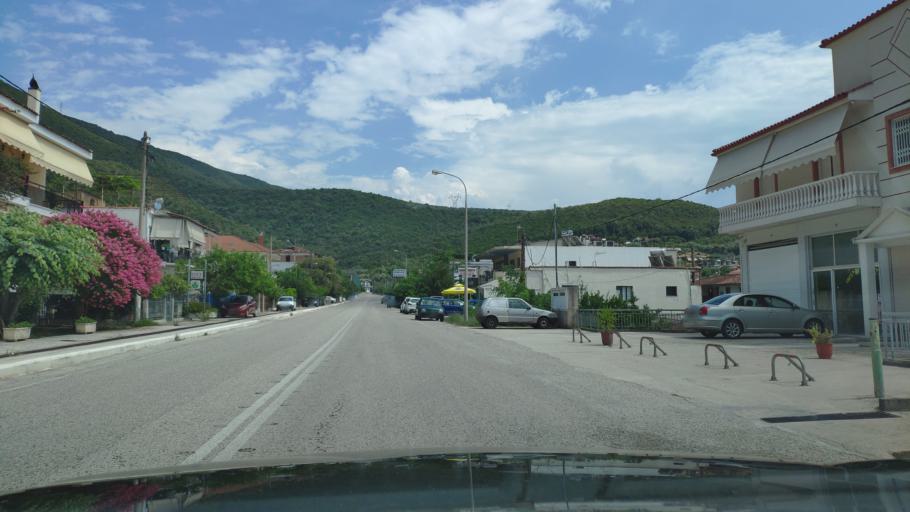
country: GR
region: West Greece
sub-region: Nomos Aitolias kai Akarnanias
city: Menidi
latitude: 39.0424
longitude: 21.1184
